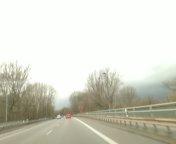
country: DE
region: North Rhine-Westphalia
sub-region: Regierungsbezirk Koln
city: Bonn
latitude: 50.7656
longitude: 7.1078
